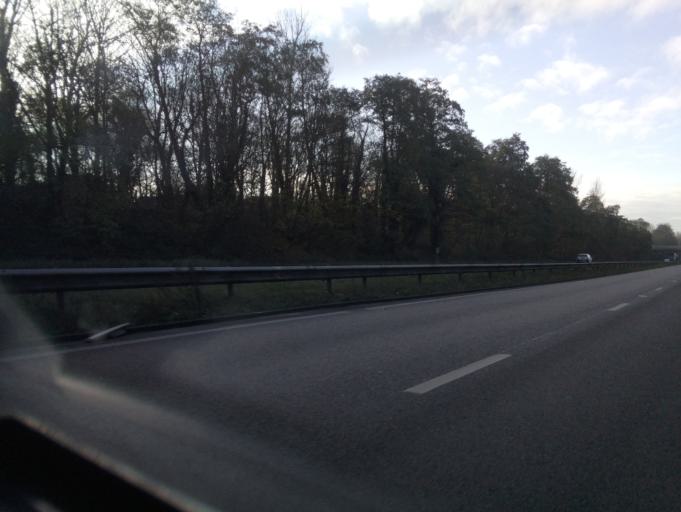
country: GB
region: England
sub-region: Staffordshire
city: Burton upon Trent
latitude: 52.8345
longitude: -1.6191
